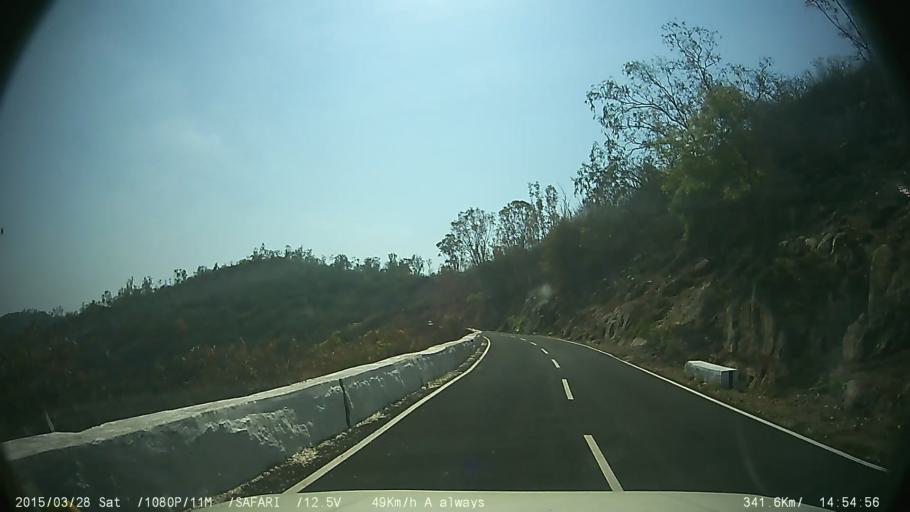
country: IN
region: Karnataka
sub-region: Mysore
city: Mysore
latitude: 12.2820
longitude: 76.6911
